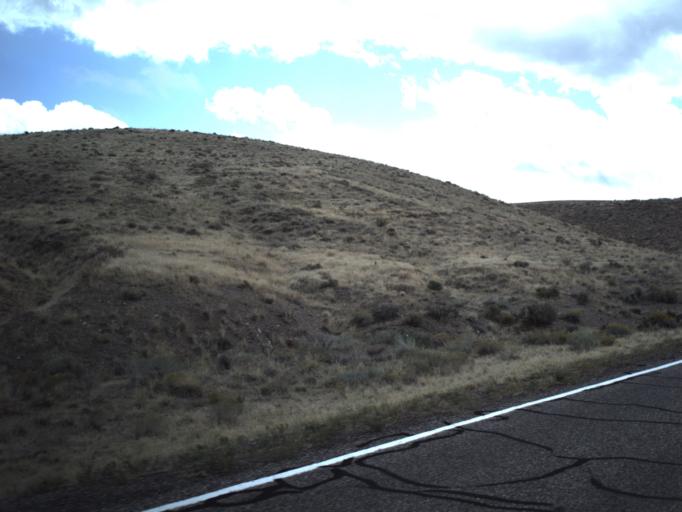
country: US
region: Utah
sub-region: Sevier County
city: Monroe
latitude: 38.6324
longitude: -112.1867
